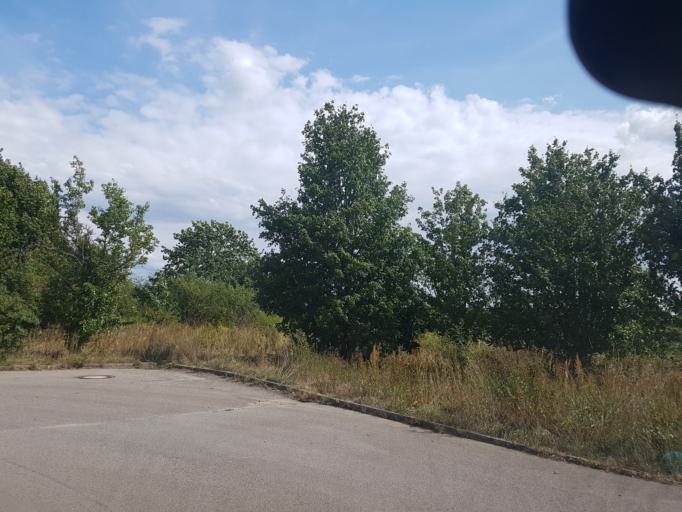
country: DE
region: Brandenburg
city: Herzberg
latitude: 51.6761
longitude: 13.2275
